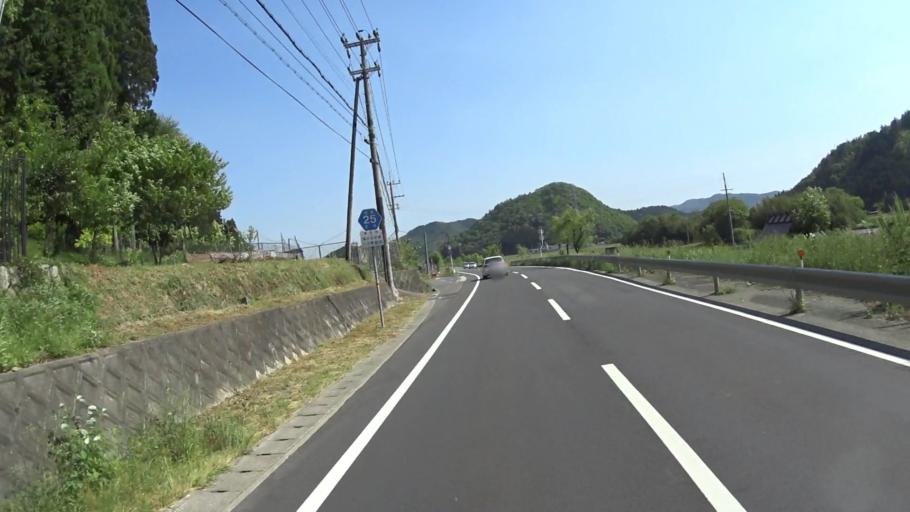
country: JP
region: Kyoto
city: Kameoka
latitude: 35.1135
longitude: 135.5185
